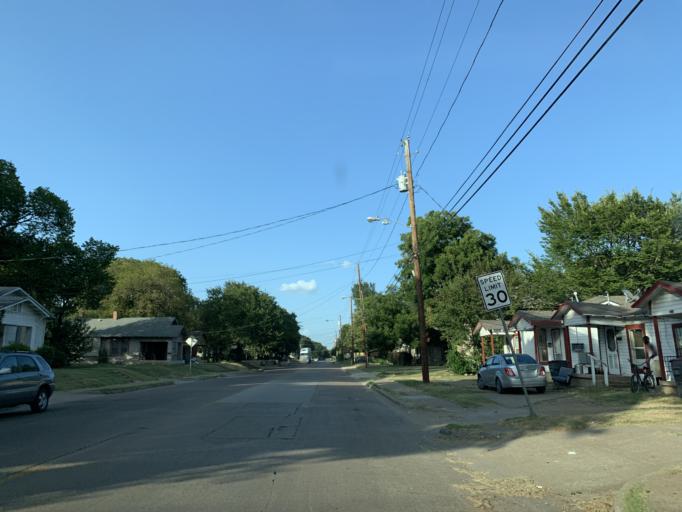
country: US
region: Texas
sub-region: Dallas County
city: Dallas
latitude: 32.7538
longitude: -96.7638
